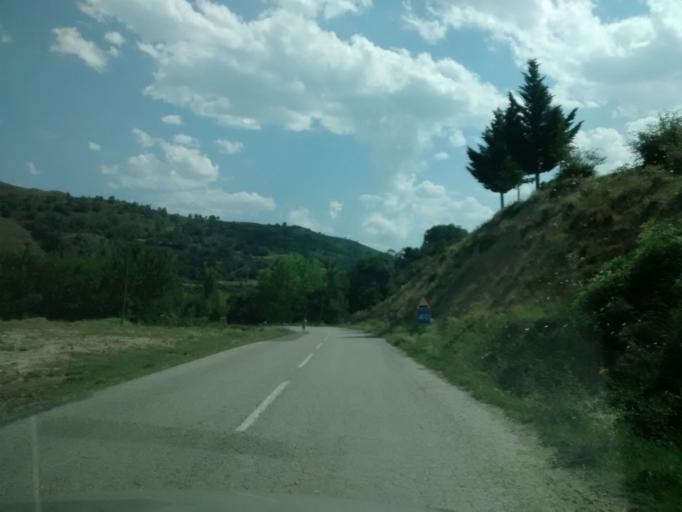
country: ES
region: La Rioja
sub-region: Provincia de La Rioja
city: San Roman de Cameros
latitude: 42.2350
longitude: -2.4723
